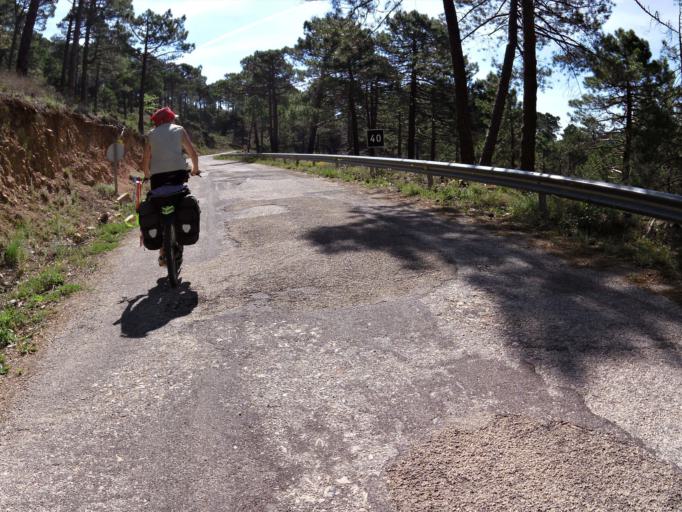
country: ES
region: Castille-La Mancha
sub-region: Provincia de Albacete
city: Riopar
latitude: 38.5238
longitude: -2.4357
